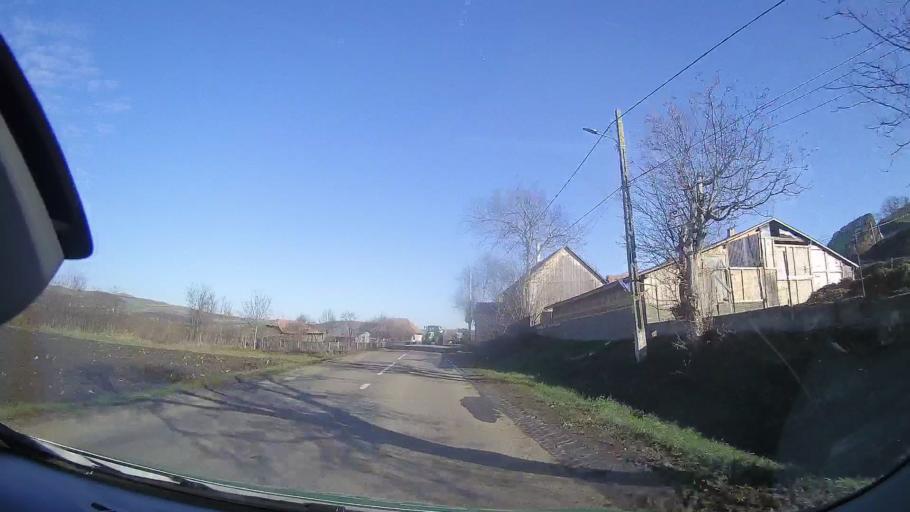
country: RO
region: Mures
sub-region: Comuna Band
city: Band
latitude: 46.5658
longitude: 24.3407
